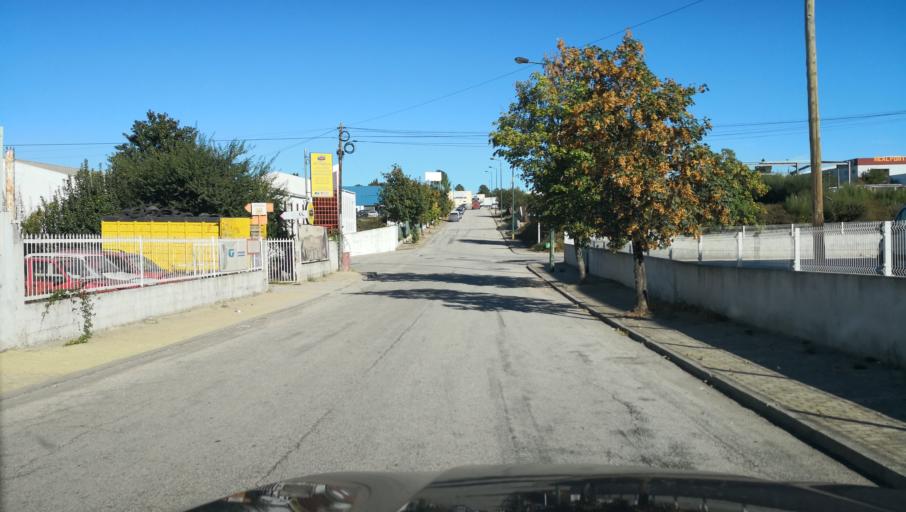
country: PT
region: Vila Real
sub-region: Vila Real
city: Vila Real
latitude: 41.2756
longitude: -7.7074
